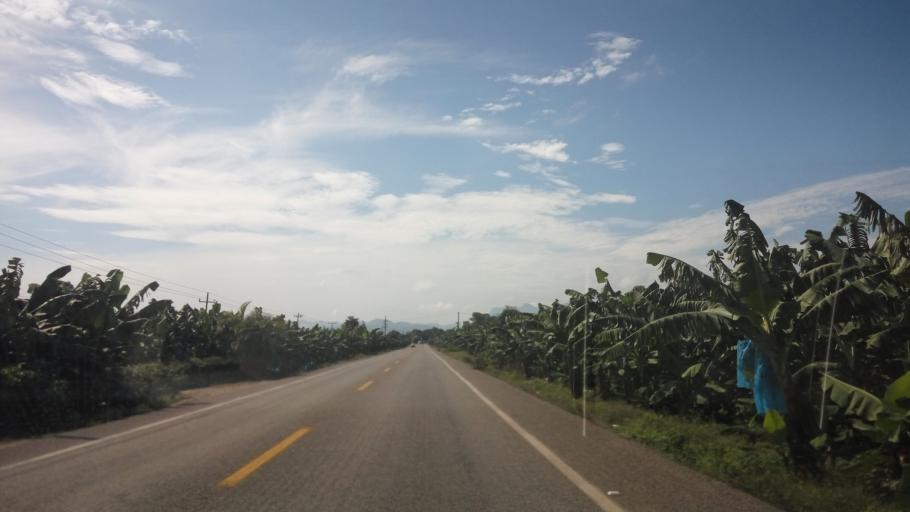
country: MX
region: Tabasco
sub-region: Teapa
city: Eureka y Belen
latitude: 17.6356
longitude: -92.9666
